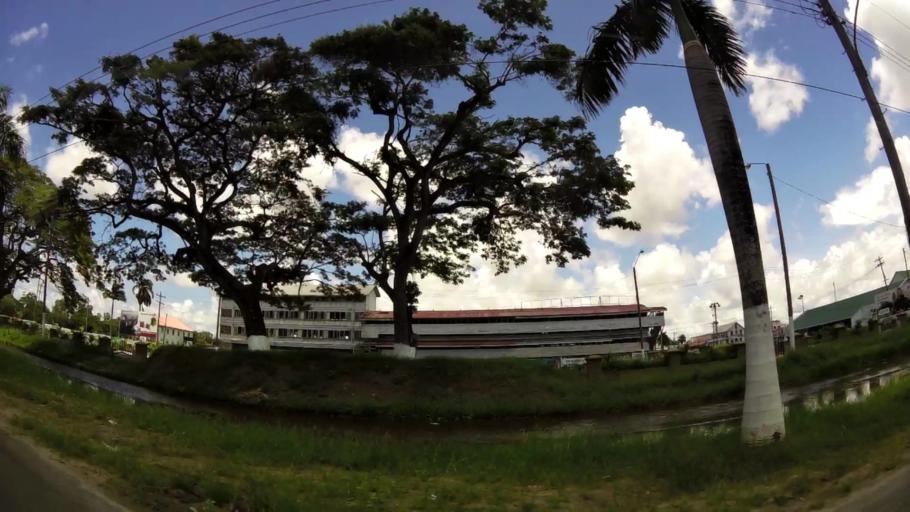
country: GY
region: Demerara-Mahaica
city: Georgetown
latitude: 6.8095
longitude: -58.1497
